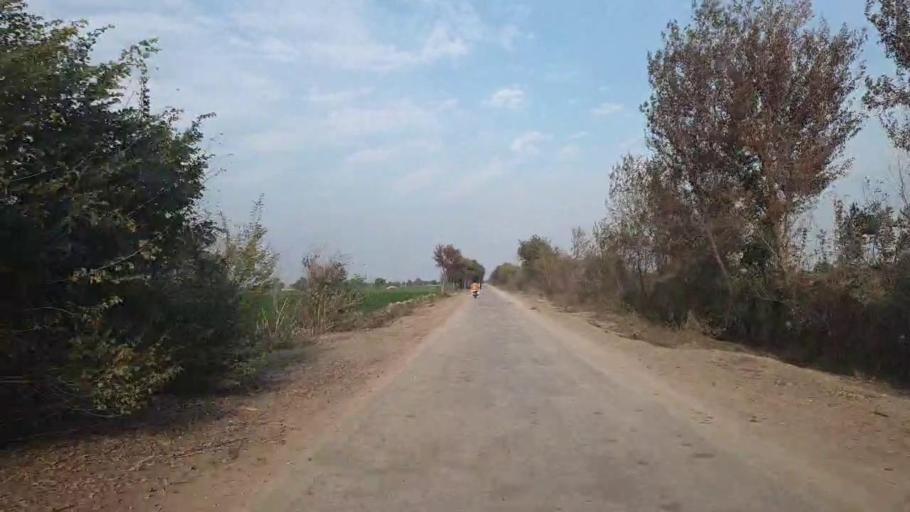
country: PK
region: Sindh
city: Shahdadpur
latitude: 26.0390
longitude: 68.5541
